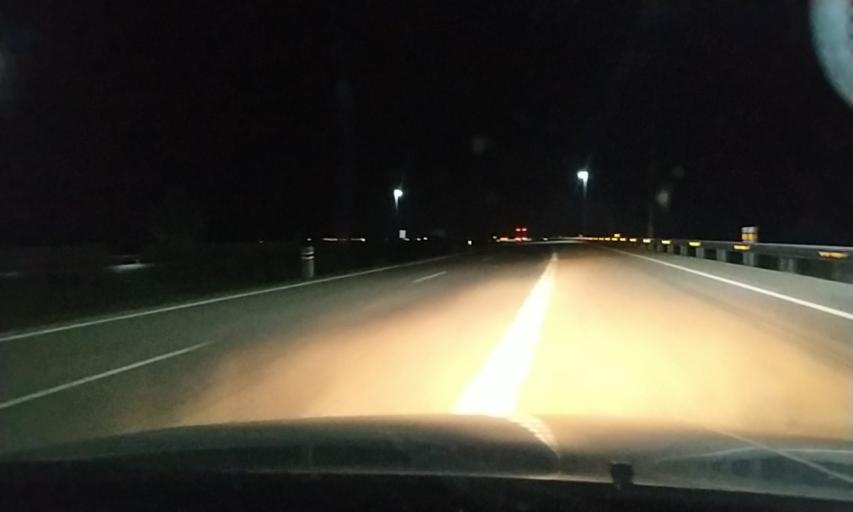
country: ES
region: Castille and Leon
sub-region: Provincia de Zamora
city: Pobladura del Valle
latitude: 42.0862
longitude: -5.7137
